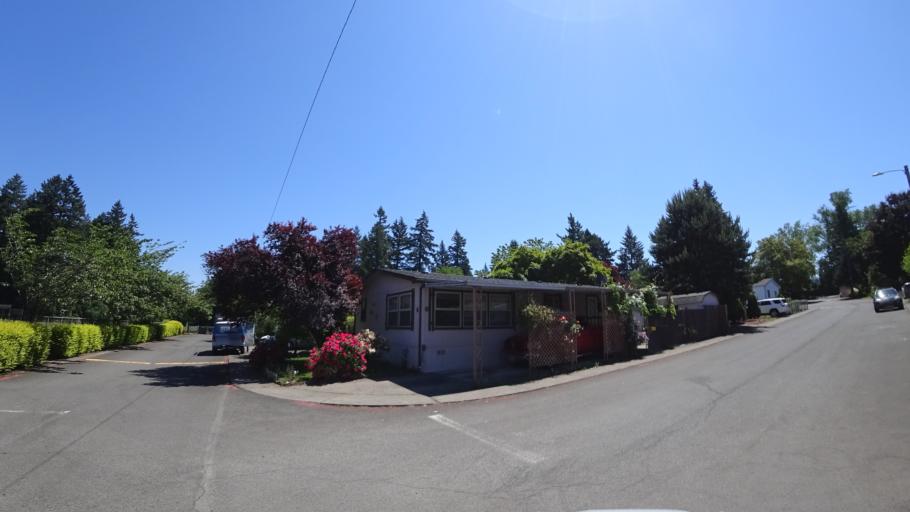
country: US
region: Oregon
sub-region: Clackamas County
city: Happy Valley
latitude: 45.4781
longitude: -122.5288
